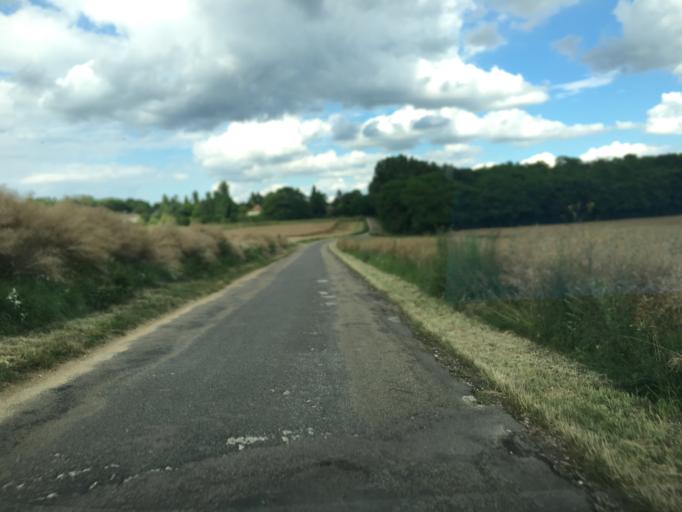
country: FR
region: Bourgogne
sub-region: Departement de l'Yonne
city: Charbuy
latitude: 47.8232
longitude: 3.4334
